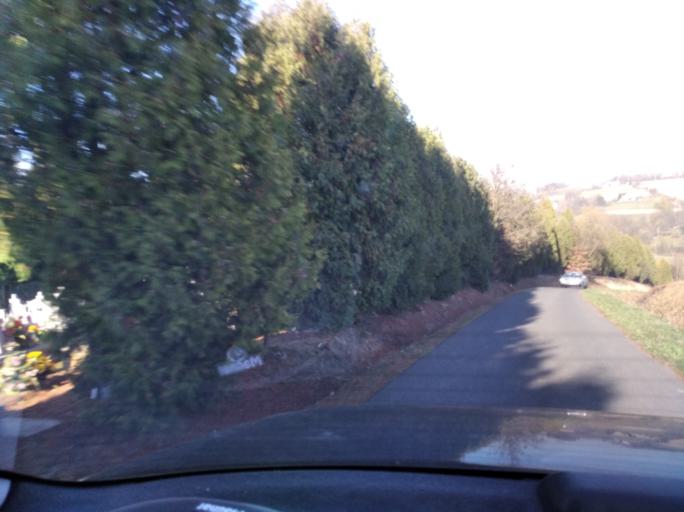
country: PL
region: Subcarpathian Voivodeship
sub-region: Powiat ropczycko-sedziszowski
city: Wielopole Skrzynskie
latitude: 49.9274
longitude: 21.5559
